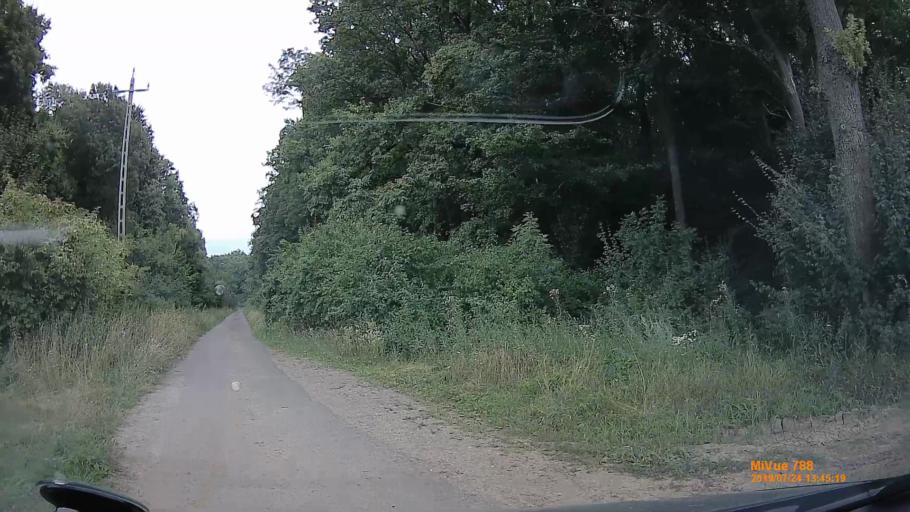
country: HU
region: Szabolcs-Szatmar-Bereg
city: Aranyosapati
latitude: 48.2644
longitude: 22.3336
